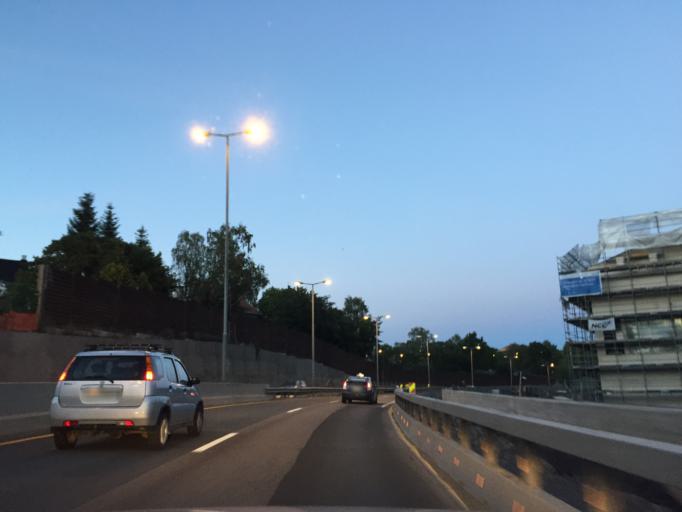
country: NO
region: Oslo
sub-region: Oslo
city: Sjolyststranda
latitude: 59.9461
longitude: 10.7064
